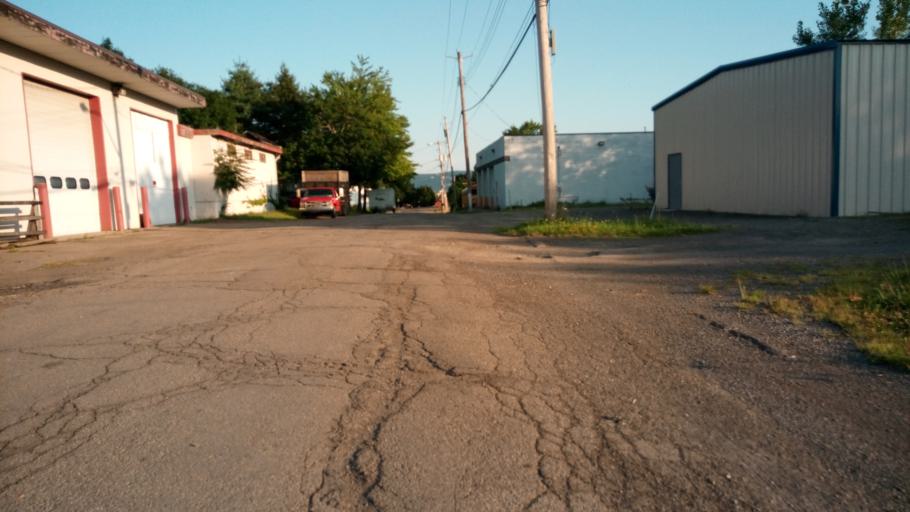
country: US
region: New York
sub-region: Chemung County
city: Elmira
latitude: 42.1016
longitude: -76.8112
